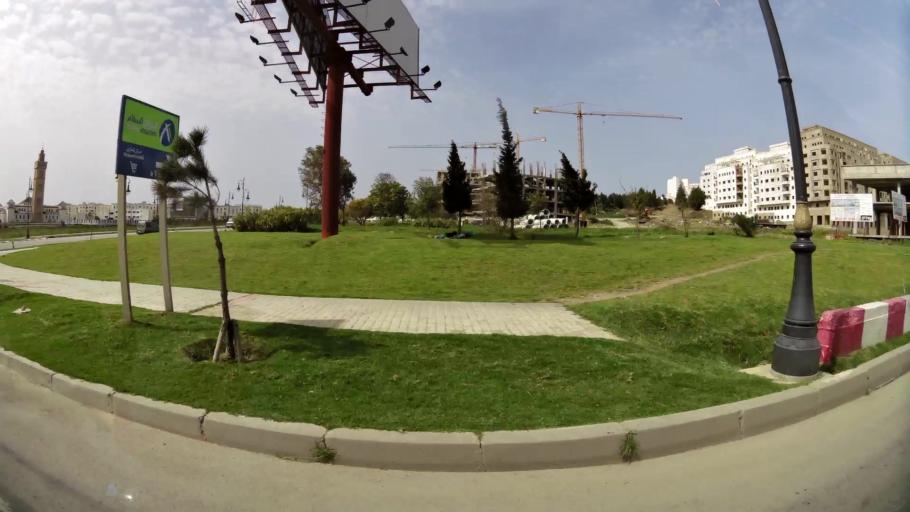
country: MA
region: Tanger-Tetouan
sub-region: Tanger-Assilah
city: Boukhalef
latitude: 35.7348
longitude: -5.8738
